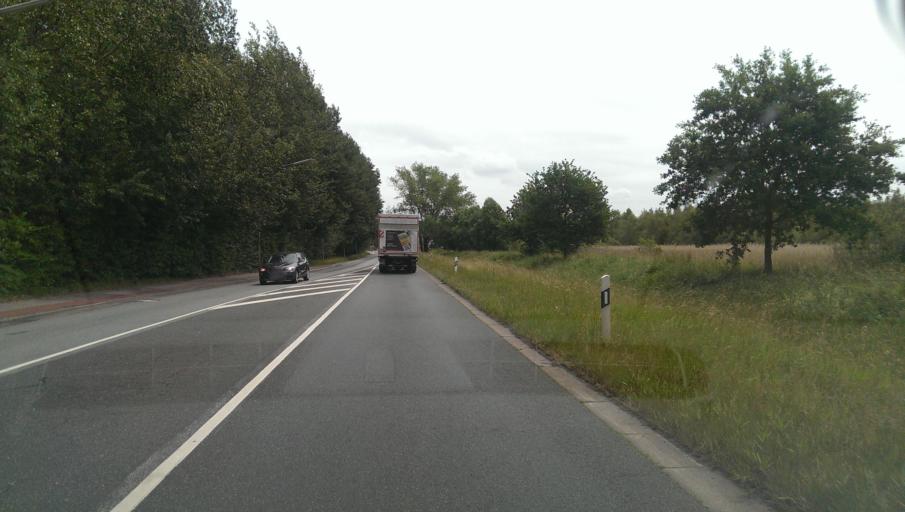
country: DE
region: Lower Saxony
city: Langen
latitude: 53.5896
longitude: 8.5593
